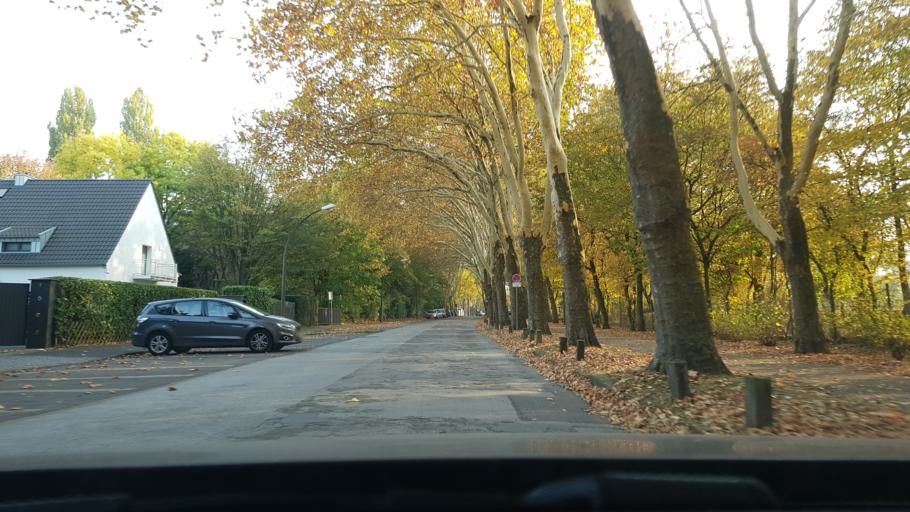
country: DE
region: North Rhine-Westphalia
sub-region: Regierungsbezirk Dusseldorf
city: Hochfeld
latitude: 51.4088
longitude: 6.7073
